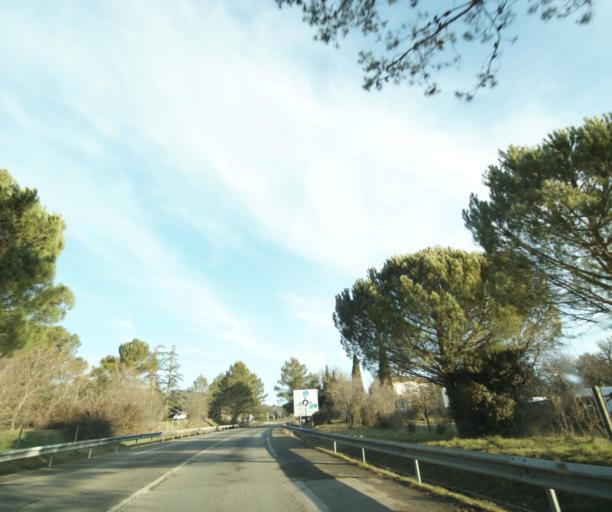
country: FR
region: Provence-Alpes-Cote d'Azur
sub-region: Departement du Var
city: Brignoles
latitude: 43.4134
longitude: 6.0618
